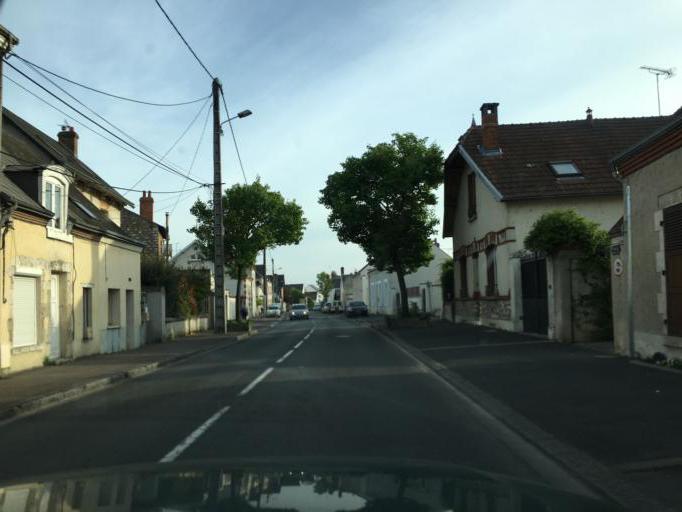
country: FR
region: Centre
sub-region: Departement du Loiret
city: Fleury-les-Aubrais
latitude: 47.9175
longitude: 1.9173
